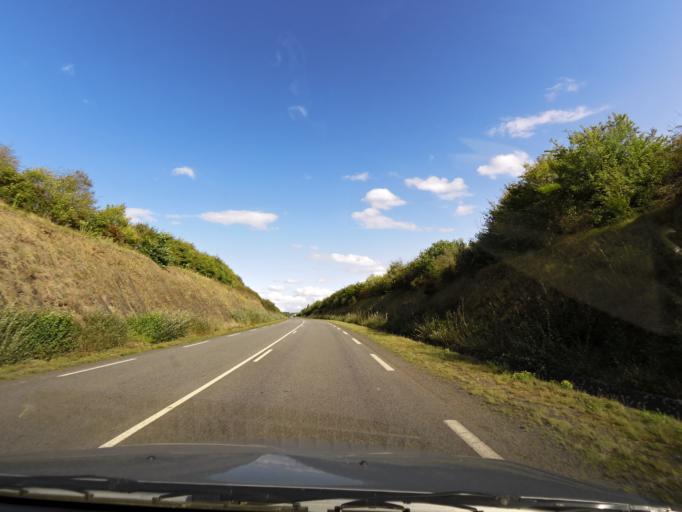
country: FR
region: Brittany
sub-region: Departement d'Ille-et-Vilaine
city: Bourg-des-Comptes
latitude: 47.9349
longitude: -1.7488
